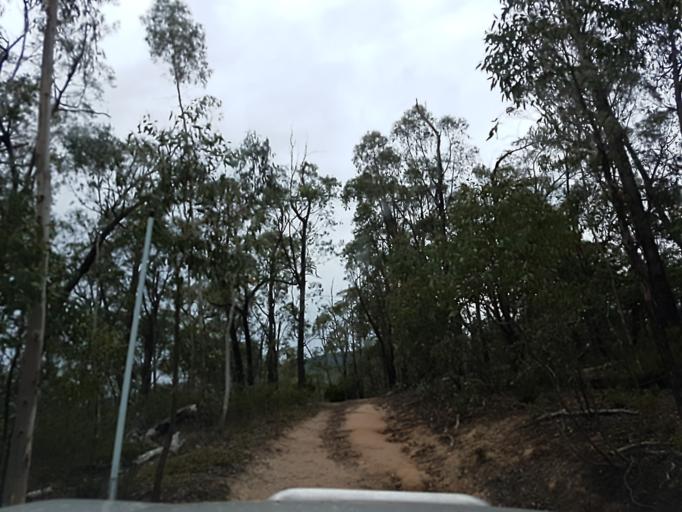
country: AU
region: New South Wales
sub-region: Snowy River
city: Jindabyne
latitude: -36.8552
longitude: 148.3335
